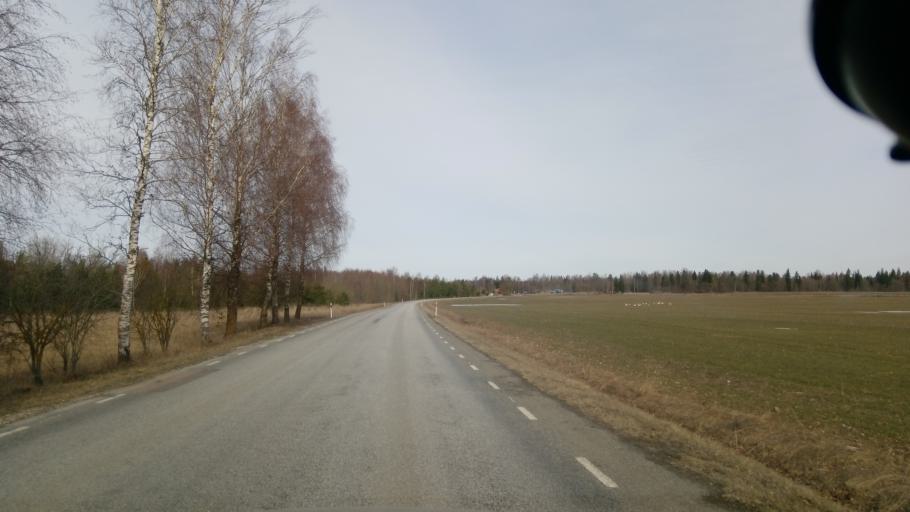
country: EE
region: Raplamaa
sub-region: Rapla vald
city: Rapla
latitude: 59.0345
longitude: 24.8355
